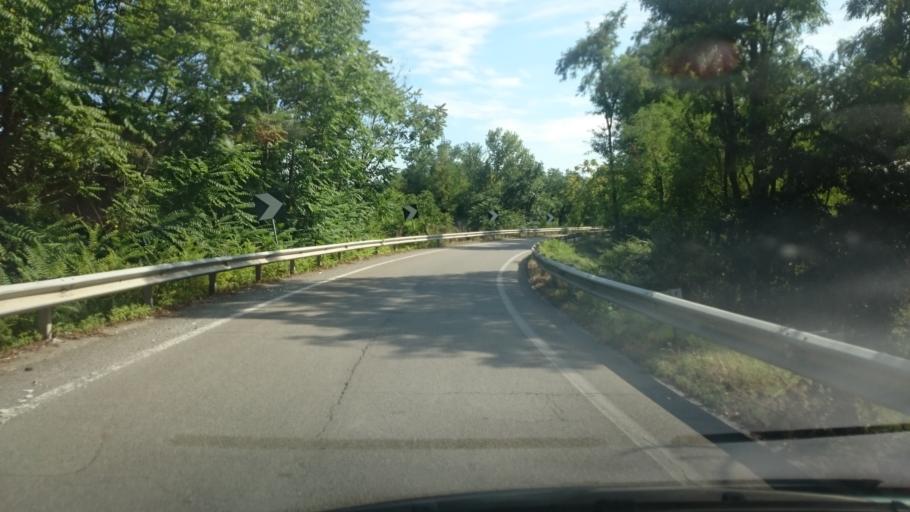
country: IT
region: Emilia-Romagna
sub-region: Provincia di Reggio Emilia
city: Veggia-Villalunga
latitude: 44.5600
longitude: 10.7672
